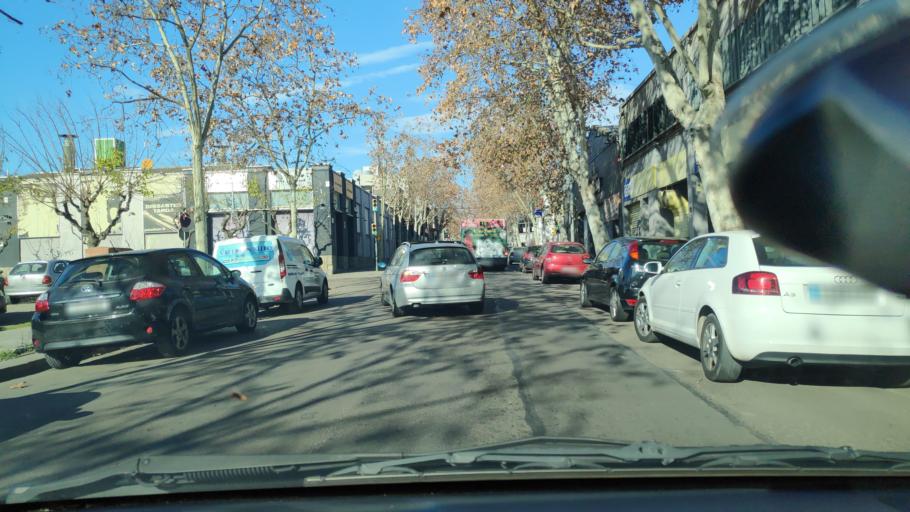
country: ES
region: Catalonia
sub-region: Provincia de Barcelona
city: Sabadell
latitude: 41.5339
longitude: 2.0995
